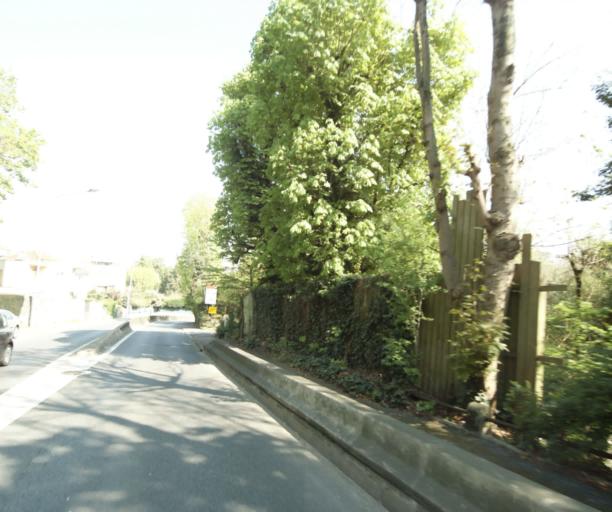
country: FR
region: Ile-de-France
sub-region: Departement des Hauts-de-Seine
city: Sevres
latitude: 48.8146
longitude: 2.2197
